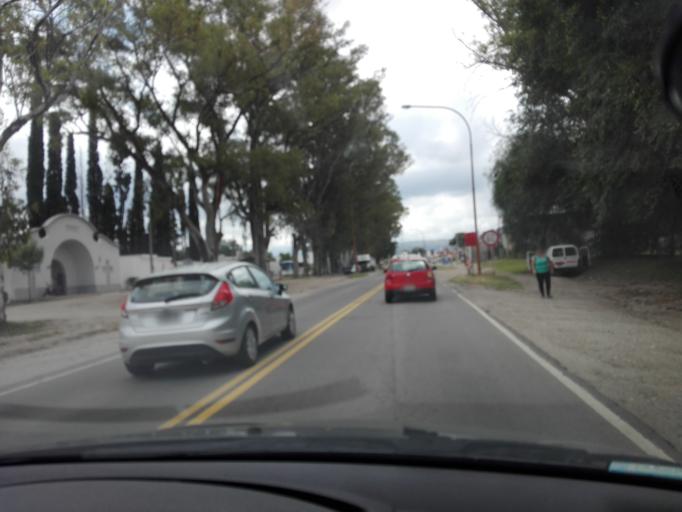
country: AR
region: Cordoba
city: Alta Gracia
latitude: -31.6583
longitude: -64.4063
